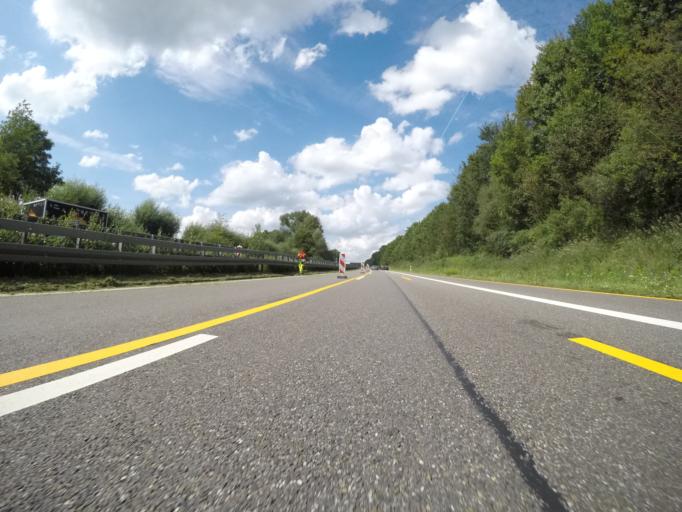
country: DE
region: Baden-Wuerttemberg
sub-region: Tuebingen Region
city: Pliezhausen
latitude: 48.5748
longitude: 9.1766
